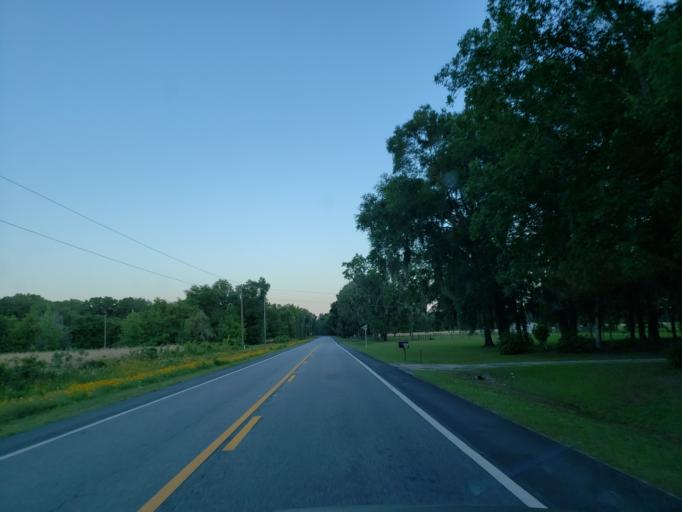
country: US
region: Georgia
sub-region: Echols County
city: Statenville
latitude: 30.5580
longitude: -83.1271
